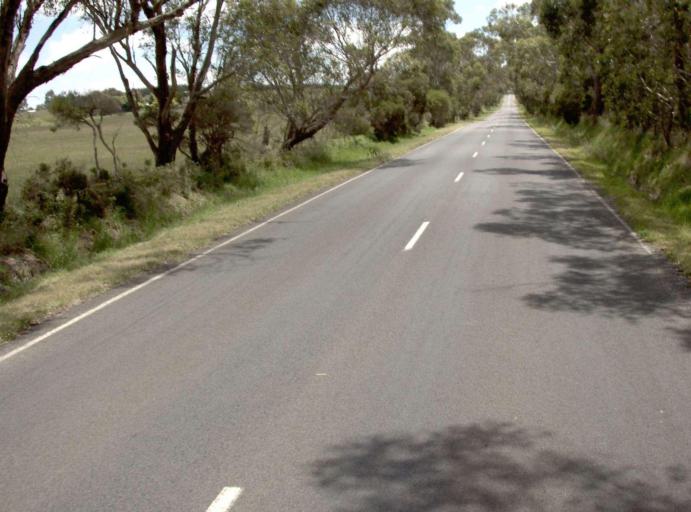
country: AU
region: Victoria
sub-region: Bass Coast
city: North Wonthaggi
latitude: -38.5954
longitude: 146.0202
